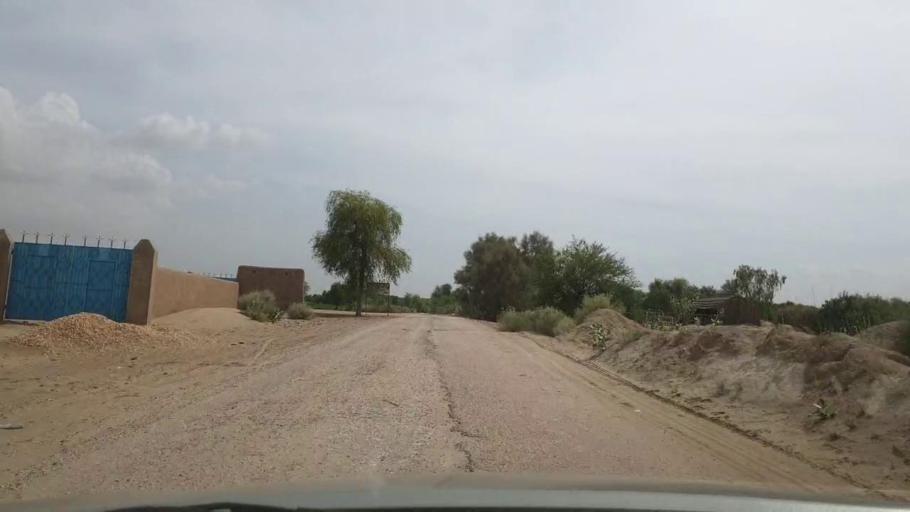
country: PK
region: Sindh
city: Kot Diji
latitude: 27.1196
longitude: 69.0256
